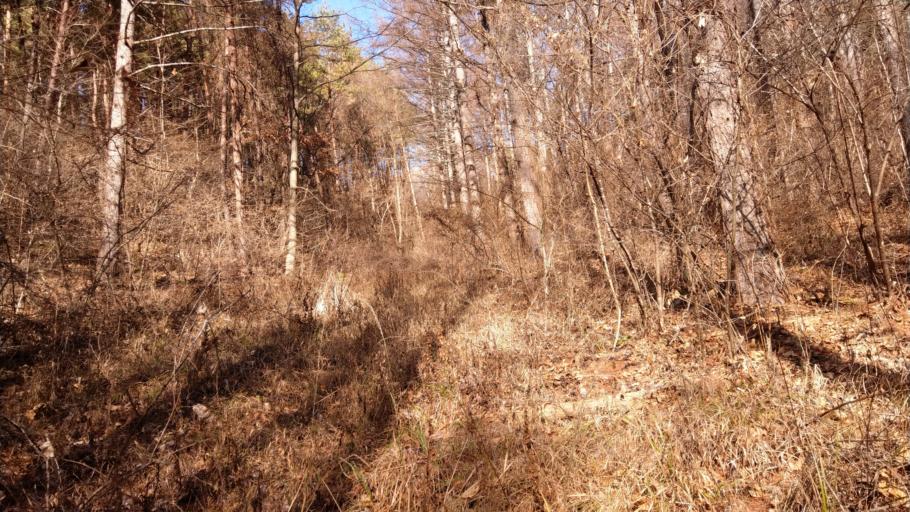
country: JP
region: Nagano
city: Komoro
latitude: 36.3773
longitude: 138.4365
